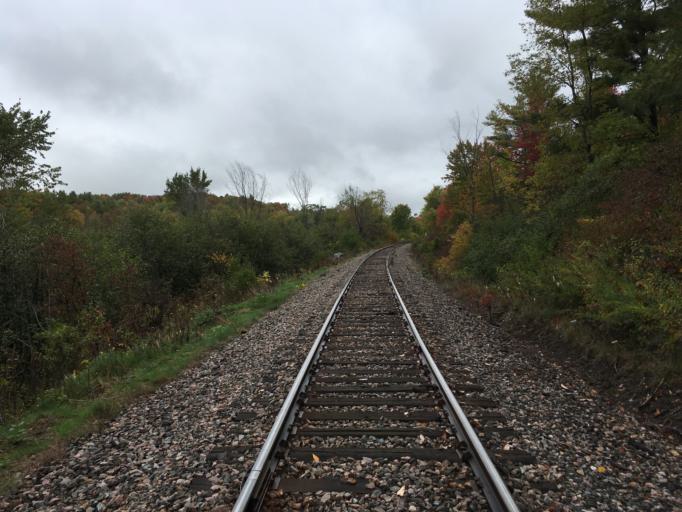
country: US
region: Vermont
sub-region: Orleans County
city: Newport
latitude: 44.8665
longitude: -72.2049
